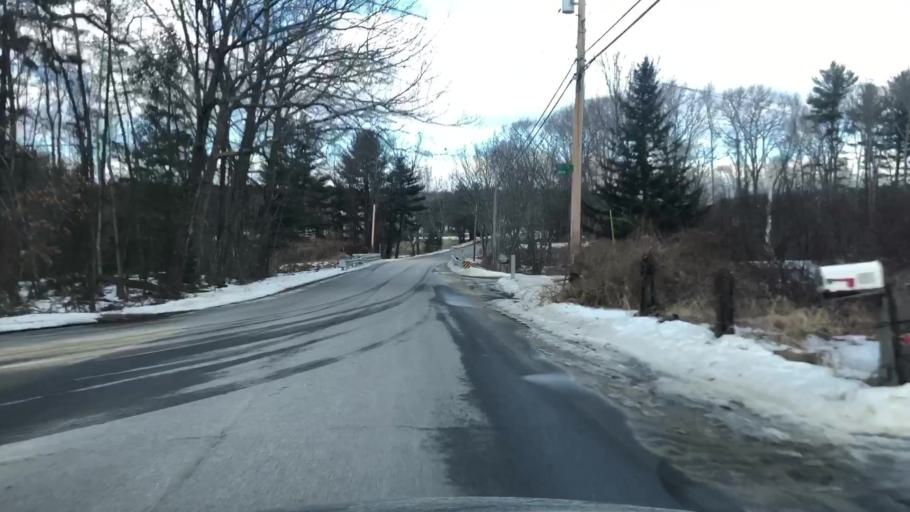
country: US
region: New Hampshire
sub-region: Hillsborough County
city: Milford
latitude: 42.8500
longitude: -71.6722
